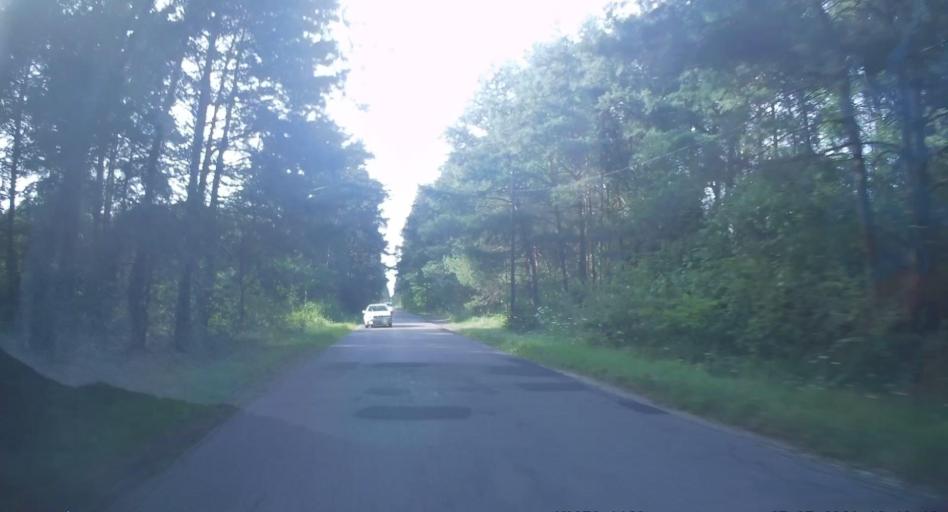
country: PL
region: Swietokrzyskie
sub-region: Powiat konecki
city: Konskie
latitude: 51.2191
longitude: 20.3895
